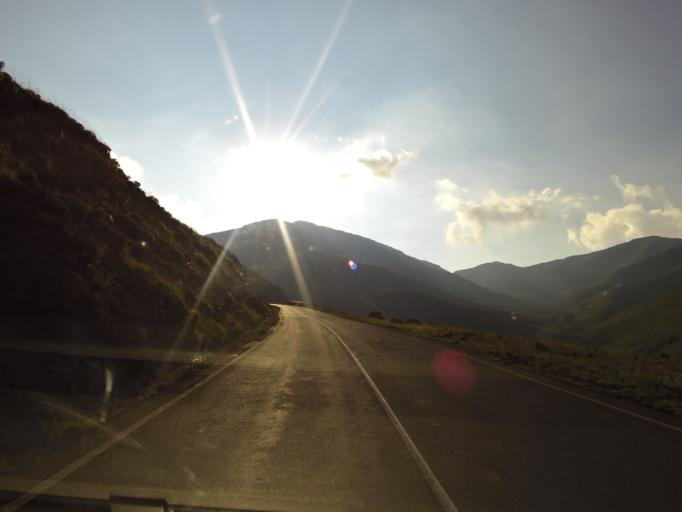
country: LS
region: Butha-Buthe
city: Butha-Buthe
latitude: -29.1123
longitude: 28.4522
